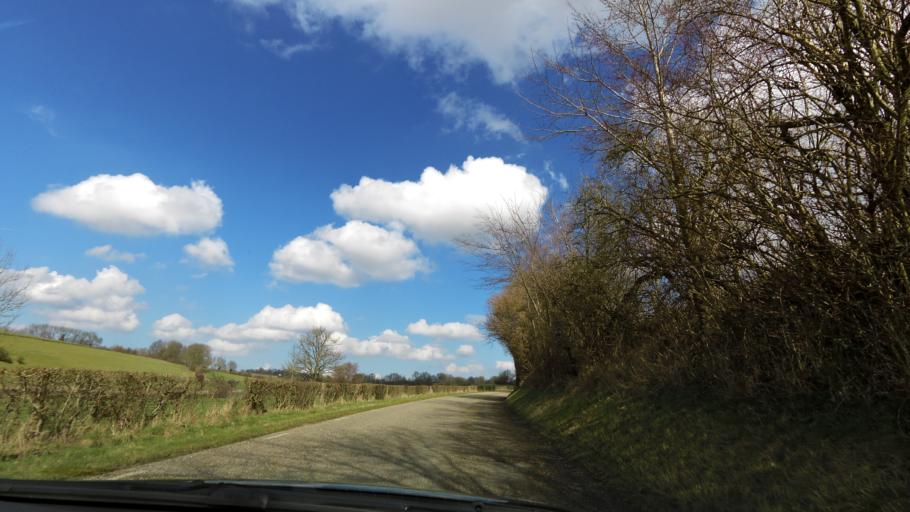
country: NL
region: Limburg
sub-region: Gemeente Voerendaal
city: Ubachsberg
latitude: 50.8310
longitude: 5.9349
